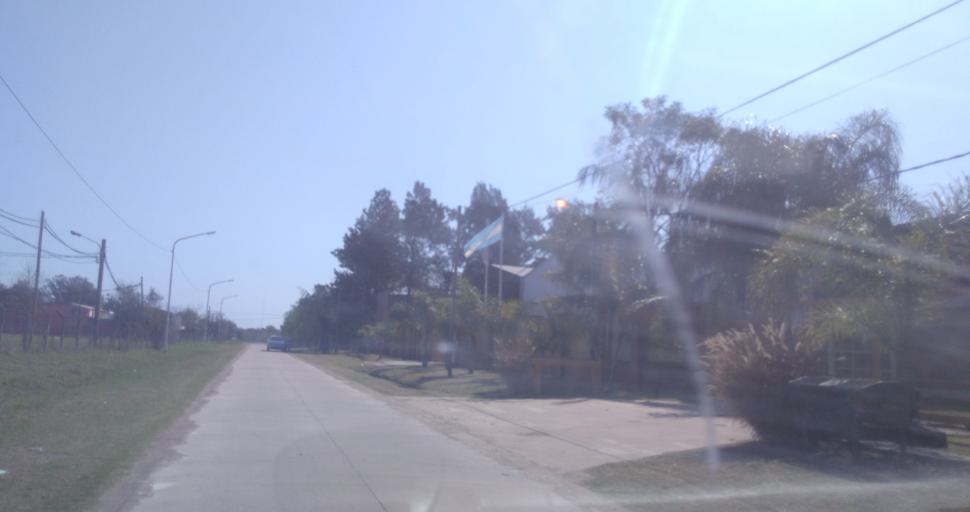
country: AR
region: Chaco
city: Fontana
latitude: -27.4314
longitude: -59.0286
